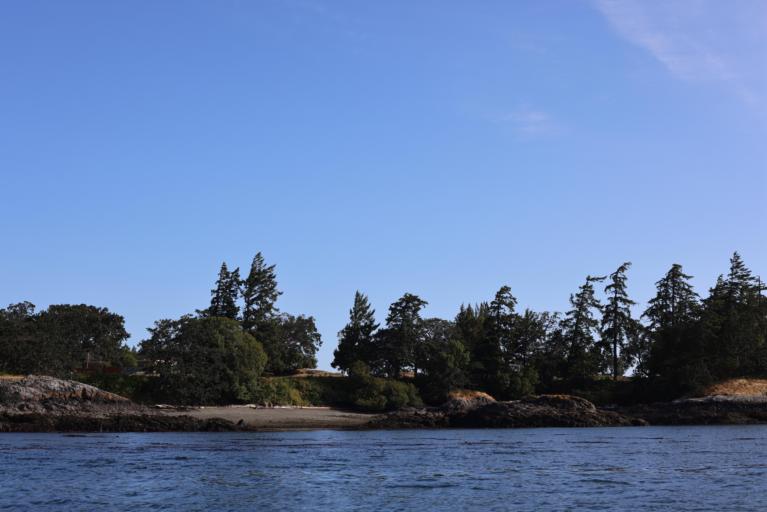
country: CA
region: British Columbia
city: Metchosin
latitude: 48.3365
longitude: -123.5400
